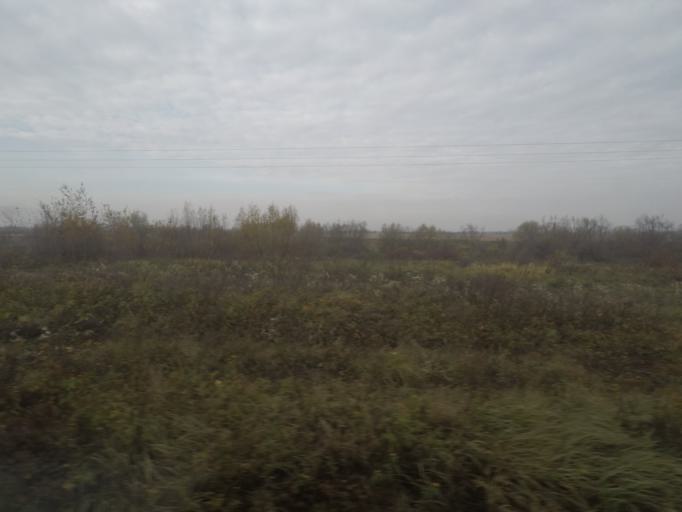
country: PL
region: Subcarpathian Voivodeship
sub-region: Powiat przemyski
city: Medyka
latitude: 49.7952
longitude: 22.8959
